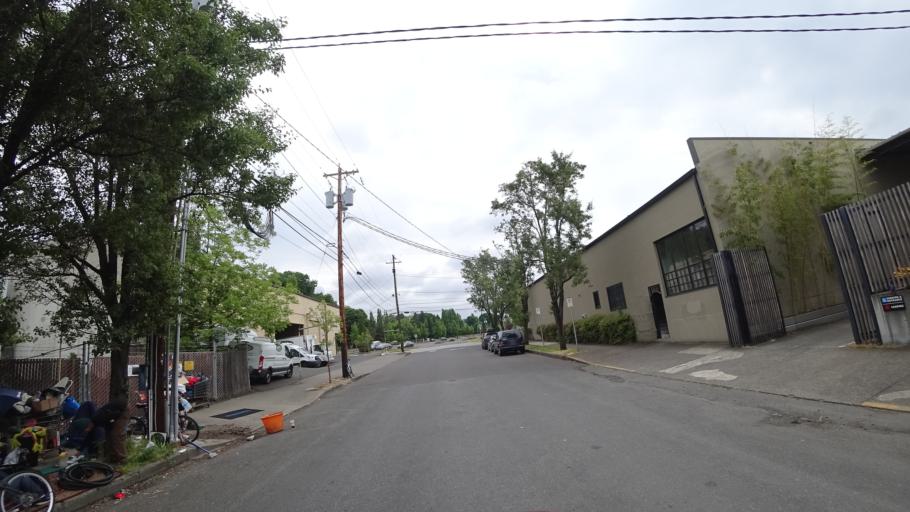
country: US
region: Oregon
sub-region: Multnomah County
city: Portland
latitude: 45.4971
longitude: -122.6444
